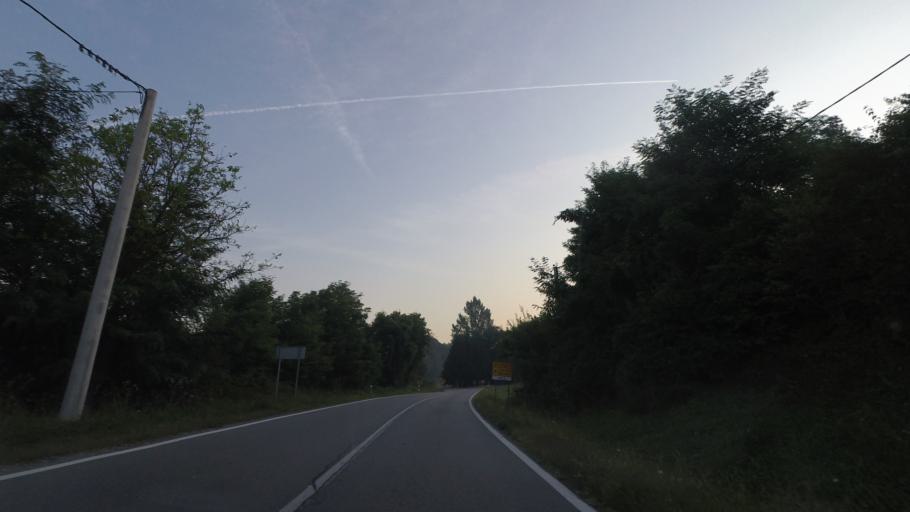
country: HR
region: Brodsko-Posavska
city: Cernik
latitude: 45.3119
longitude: 17.4357
